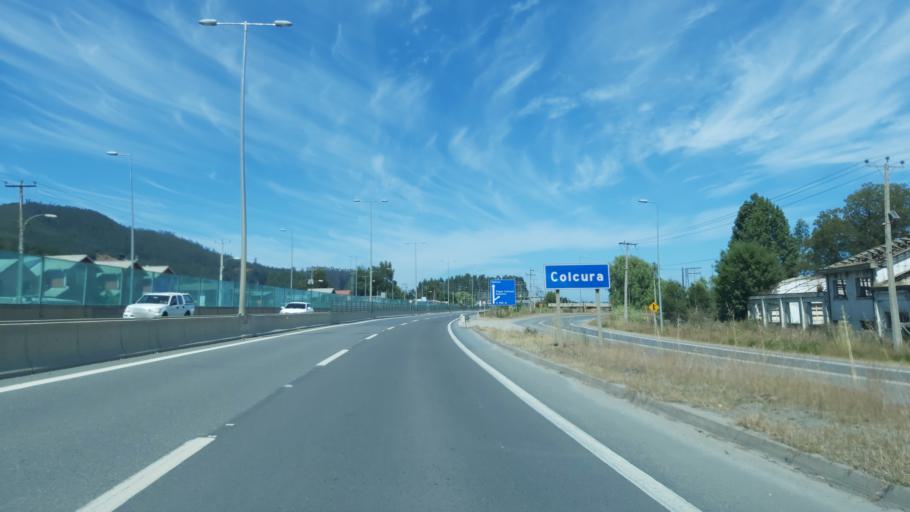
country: CL
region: Biobio
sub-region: Provincia de Concepcion
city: Lota
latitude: -37.1086
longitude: -73.1430
